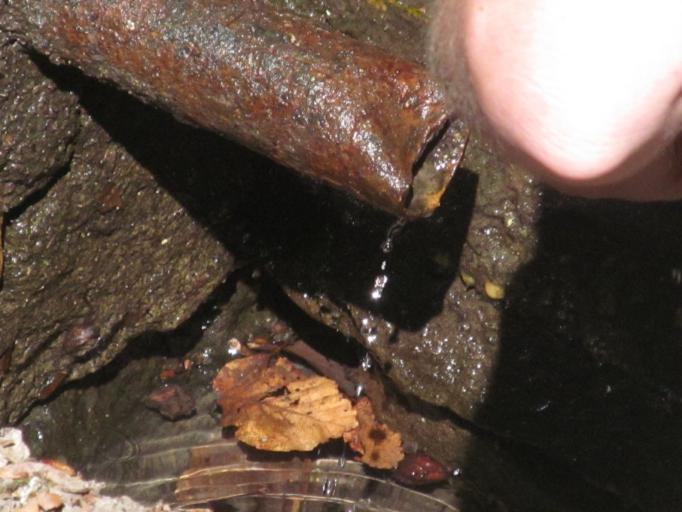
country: HU
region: Pest
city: Pilisszentkereszt
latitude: 47.7174
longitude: 18.9320
